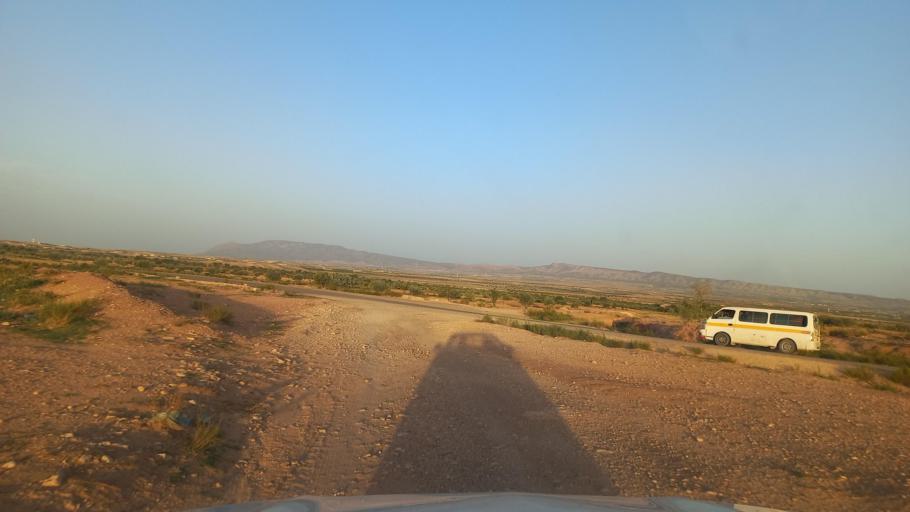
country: TN
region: Al Qasrayn
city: Sbiba
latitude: 35.3709
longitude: 9.0110
